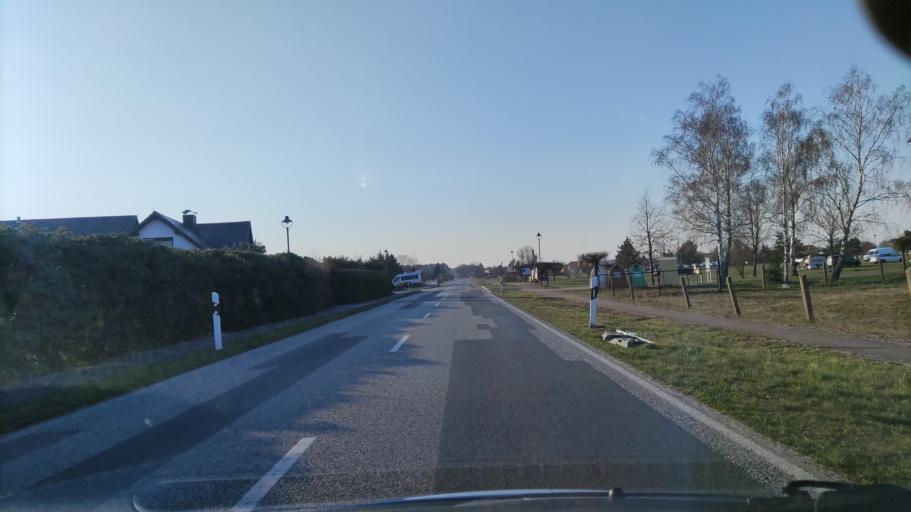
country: DE
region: Saxony-Anhalt
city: Seehausen
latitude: 52.9133
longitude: 11.7229
